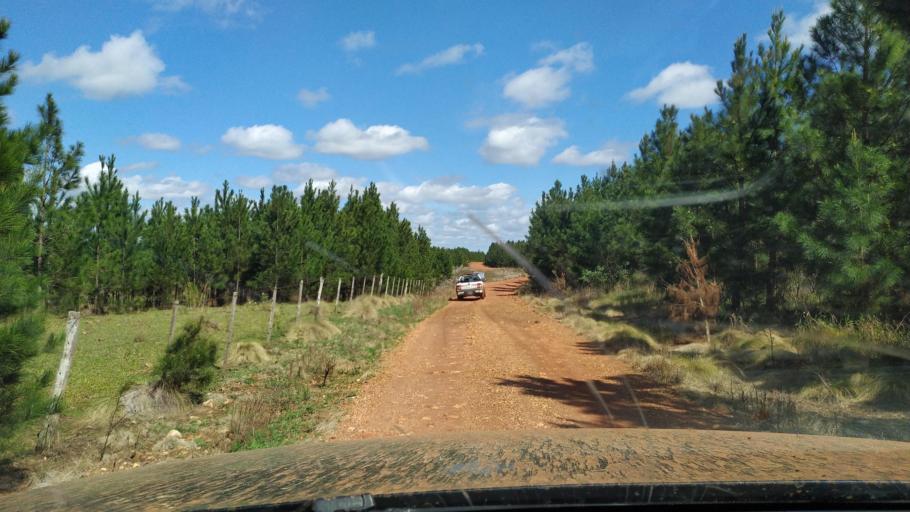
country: AR
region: Corrientes
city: Santo Tome
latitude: -28.4641
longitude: -55.9755
